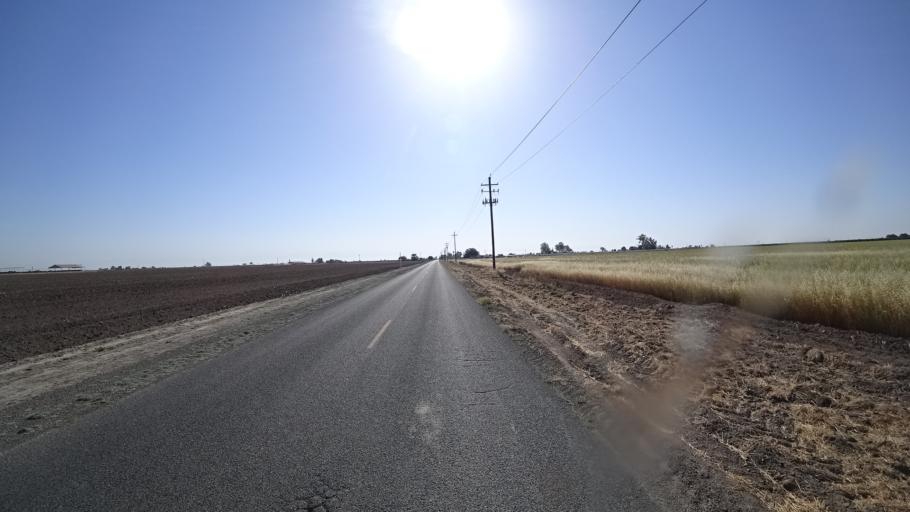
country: US
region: California
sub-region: Kings County
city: Corcoran
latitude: 36.1379
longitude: -119.5340
